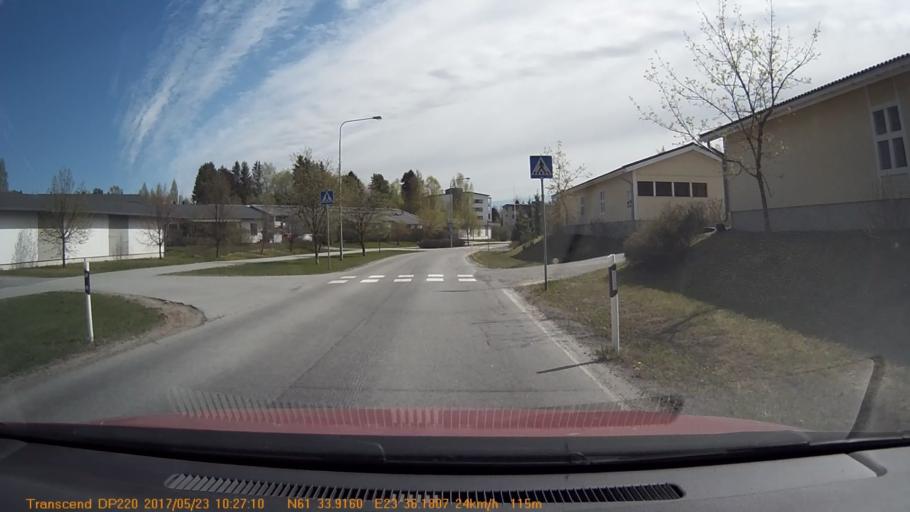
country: FI
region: Pirkanmaa
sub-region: Tampere
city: Yloejaervi
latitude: 61.5653
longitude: 23.6031
